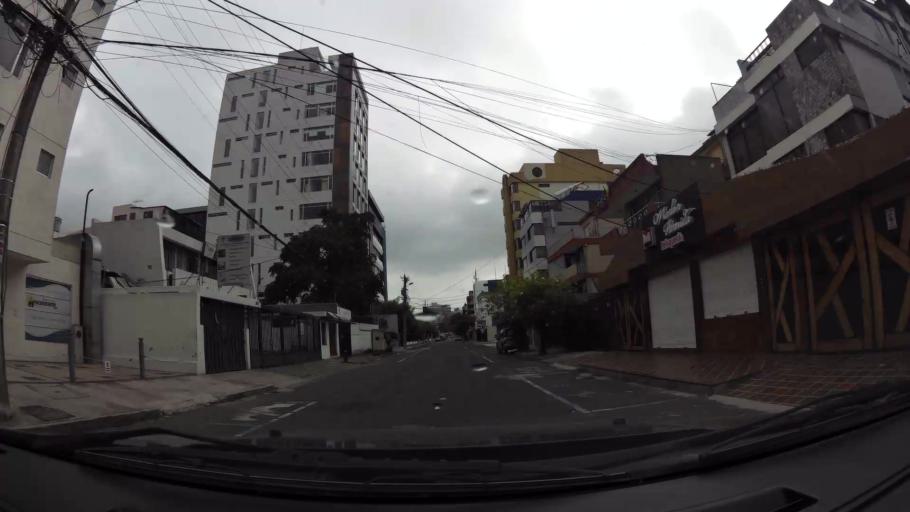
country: EC
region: Pichincha
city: Quito
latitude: -0.1911
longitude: -78.4906
